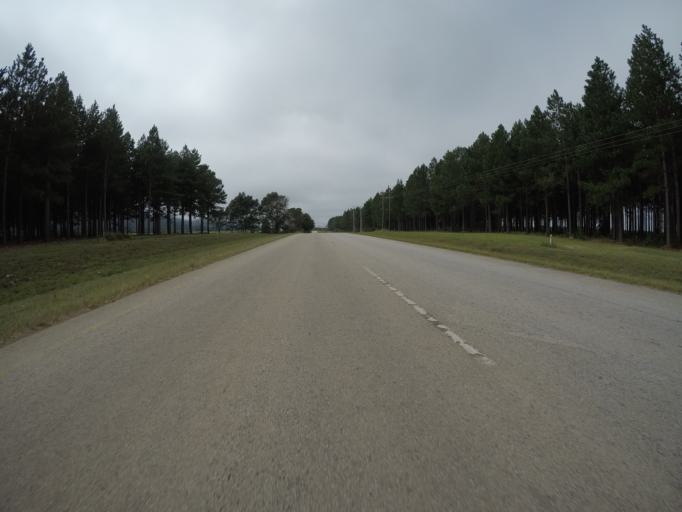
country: ZA
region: Eastern Cape
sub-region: Cacadu District Municipality
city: Kareedouw
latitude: -33.9957
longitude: 24.1309
